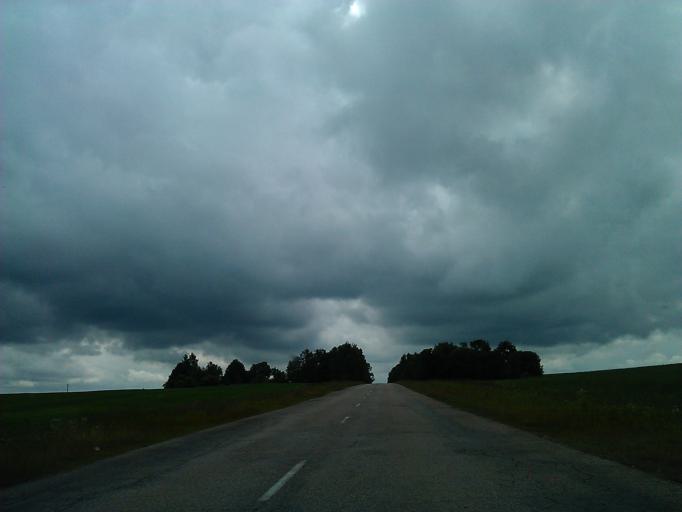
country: LV
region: Aizpute
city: Aizpute
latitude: 56.8340
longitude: 21.7544
